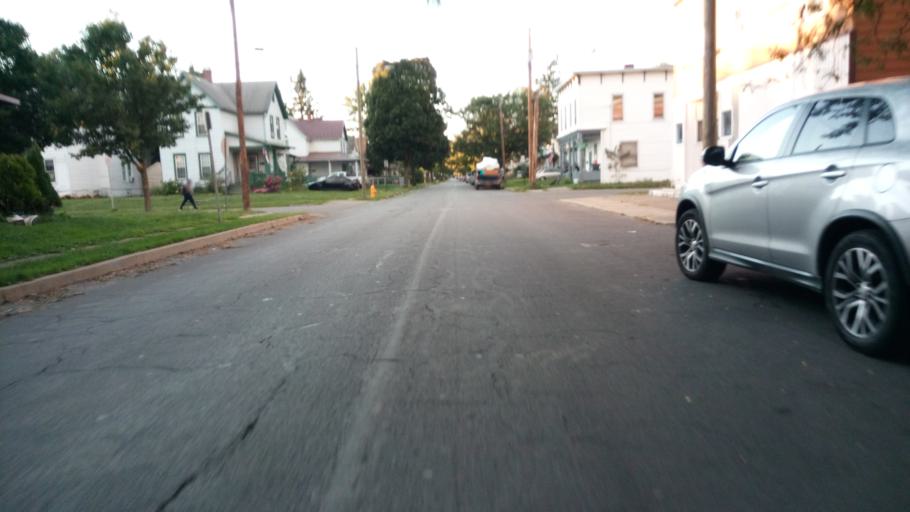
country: US
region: New York
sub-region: Chemung County
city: Elmira
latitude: 42.1031
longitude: -76.8022
